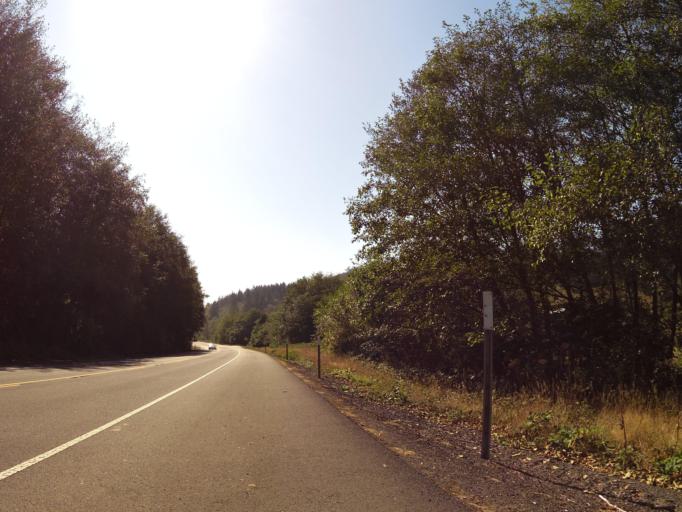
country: US
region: Oregon
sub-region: Tillamook County
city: Pacific City
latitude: 45.1570
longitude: -123.9524
